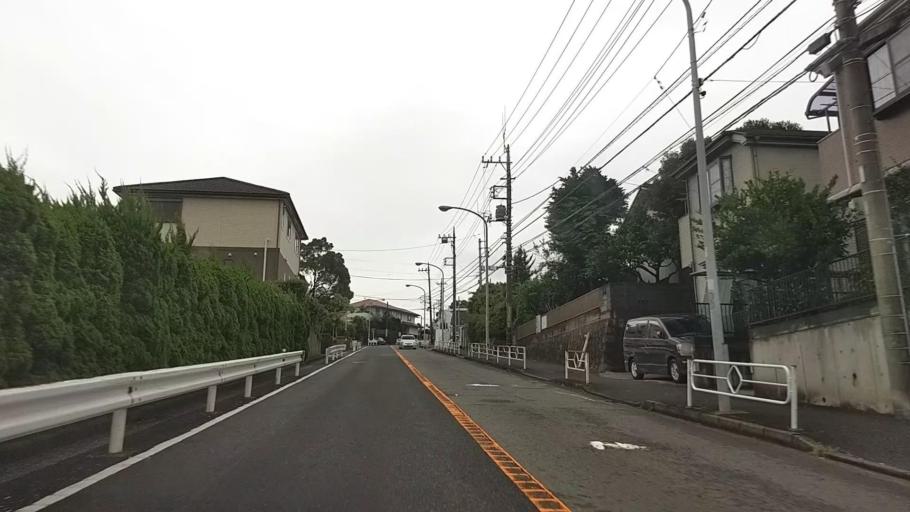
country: JP
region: Kanagawa
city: Yokohama
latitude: 35.3904
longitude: 139.5798
